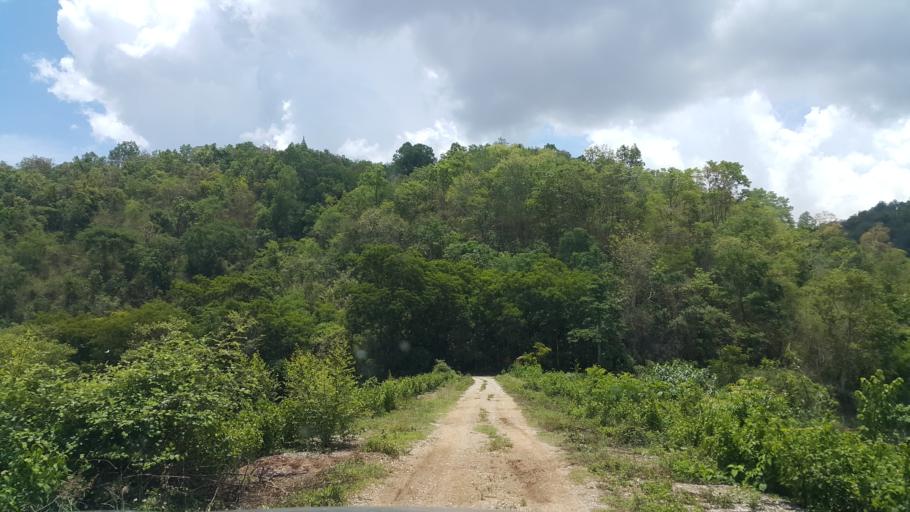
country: TH
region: Phayao
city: Phayao
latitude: 19.1851
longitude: 99.8012
